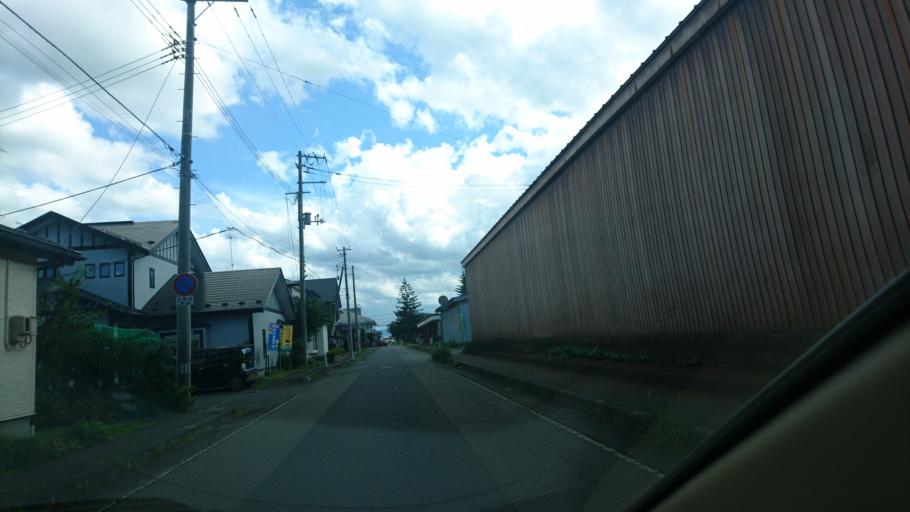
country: JP
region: Iwate
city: Mizusawa
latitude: 39.1940
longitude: 141.1744
